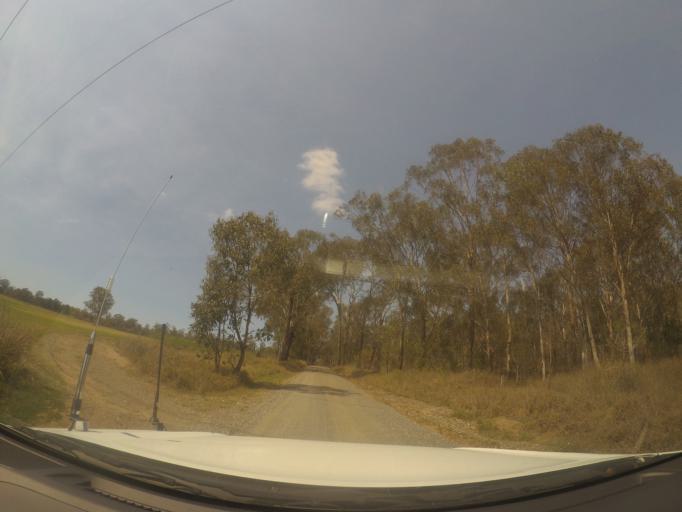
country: AU
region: Queensland
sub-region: Logan
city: North Maclean
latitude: -27.7740
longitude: 153.0382
